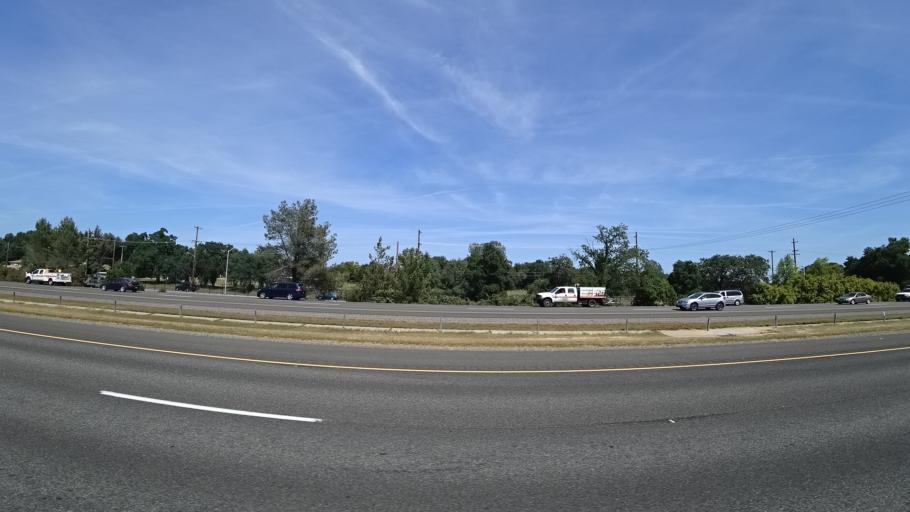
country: US
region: California
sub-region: Shasta County
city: Redding
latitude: 40.5458
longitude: -122.3536
